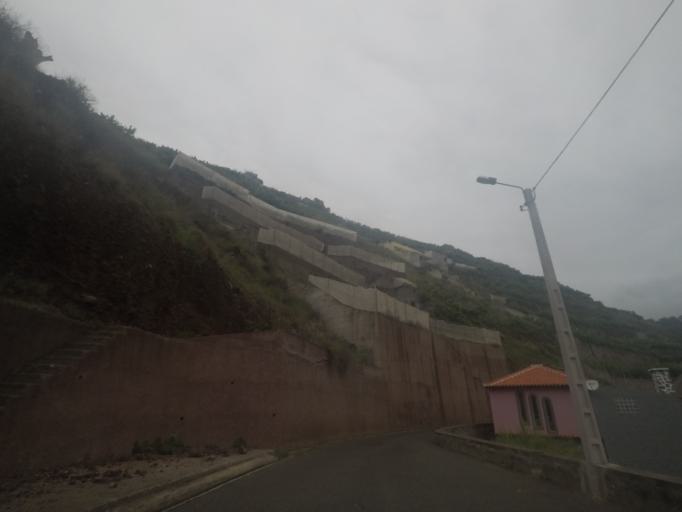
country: PT
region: Madeira
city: Camara de Lobos
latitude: 32.6592
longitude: -16.9634
